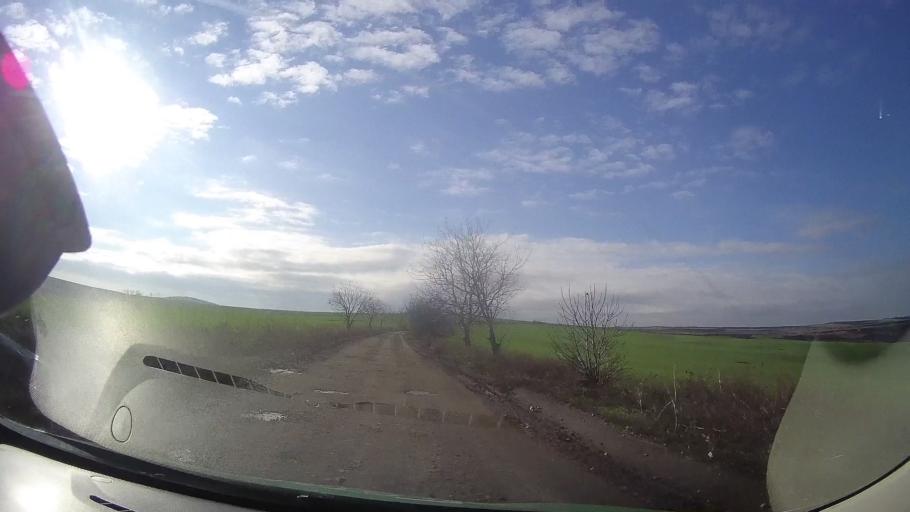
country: RO
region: Mures
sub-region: Comuna Saulia
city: Saulia
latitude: 46.6047
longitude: 24.2429
